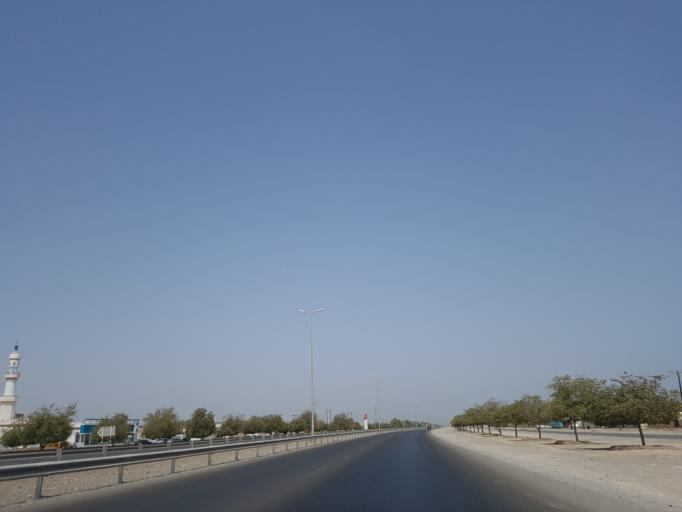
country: OM
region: Al Batinah
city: Al Khaburah
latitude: 24.0520
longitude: 56.9733
